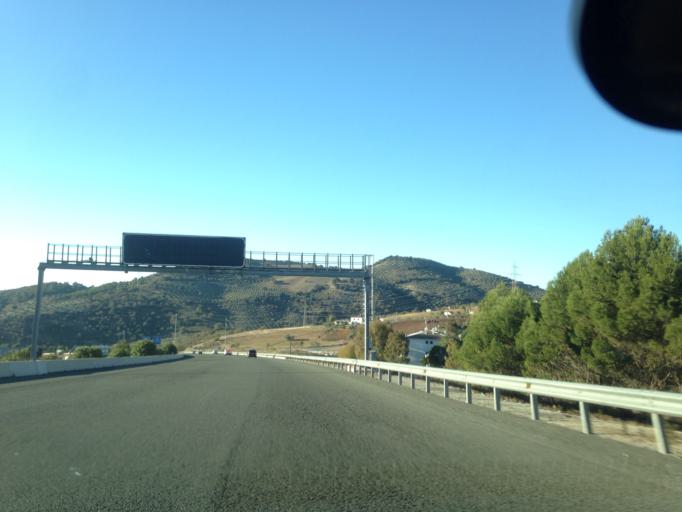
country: ES
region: Andalusia
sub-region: Provincia de Malaga
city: Casabermeja
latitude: 36.9628
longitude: -4.4459
